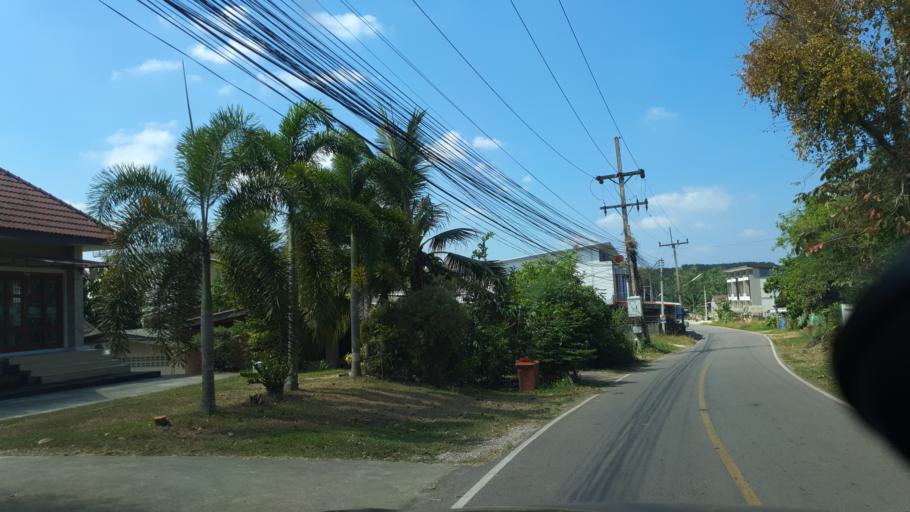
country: TH
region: Krabi
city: Nuea Khlong
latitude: 8.0838
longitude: 98.9888
